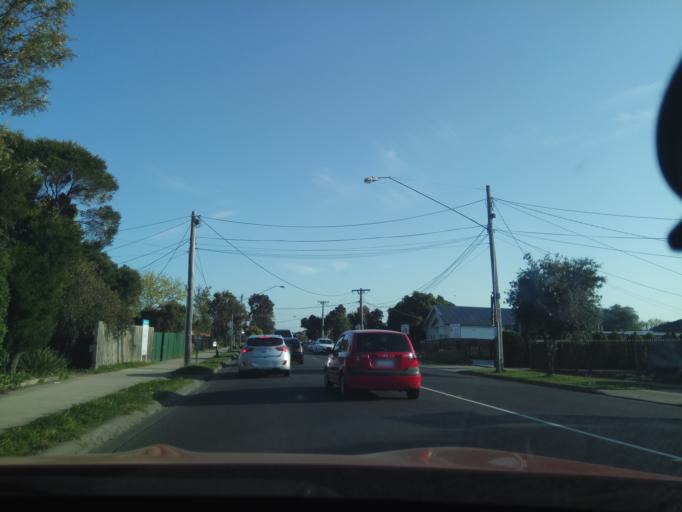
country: AU
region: Victoria
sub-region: Hobsons Bay
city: Laverton
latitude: -37.8710
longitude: 144.7600
